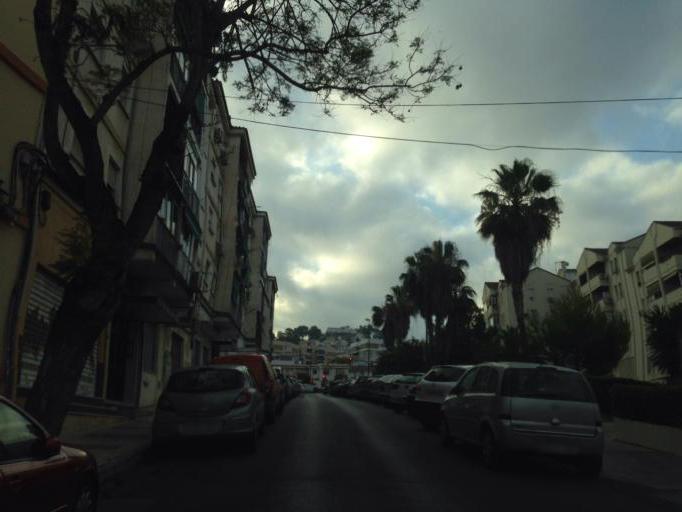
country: ES
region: Andalusia
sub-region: Provincia de Malaga
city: Malaga
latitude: 36.7466
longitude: -4.4190
